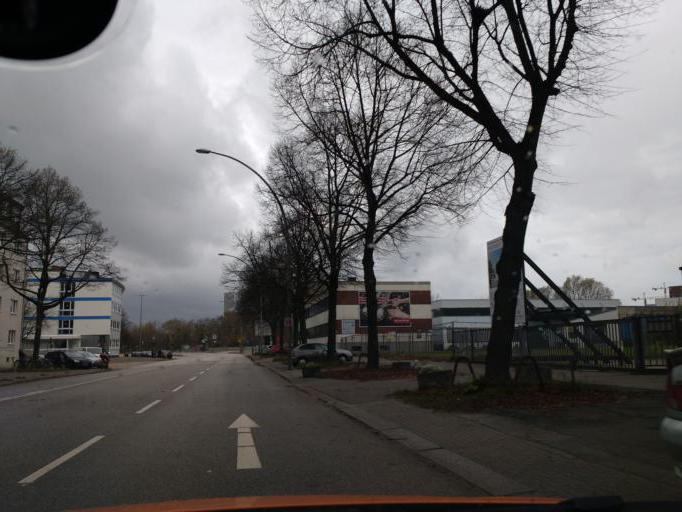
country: DE
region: Hamburg
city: Hammerbrook
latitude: 53.5414
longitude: 10.0364
